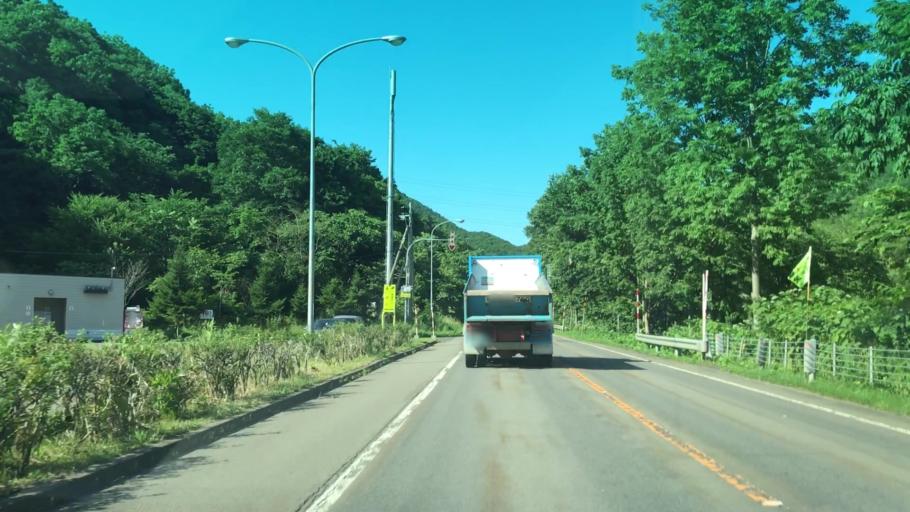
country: JP
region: Hokkaido
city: Iwanai
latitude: 43.0211
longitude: 140.6683
